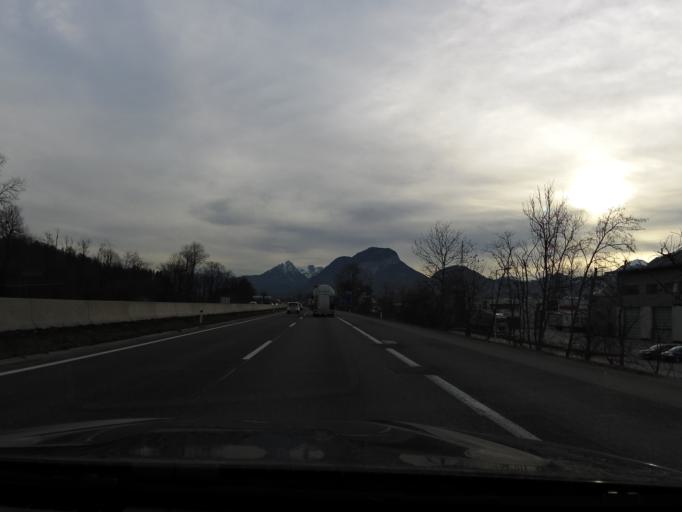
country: AT
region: Tyrol
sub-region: Politischer Bezirk Kufstein
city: Worgl
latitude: 47.4866
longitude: 12.0433
